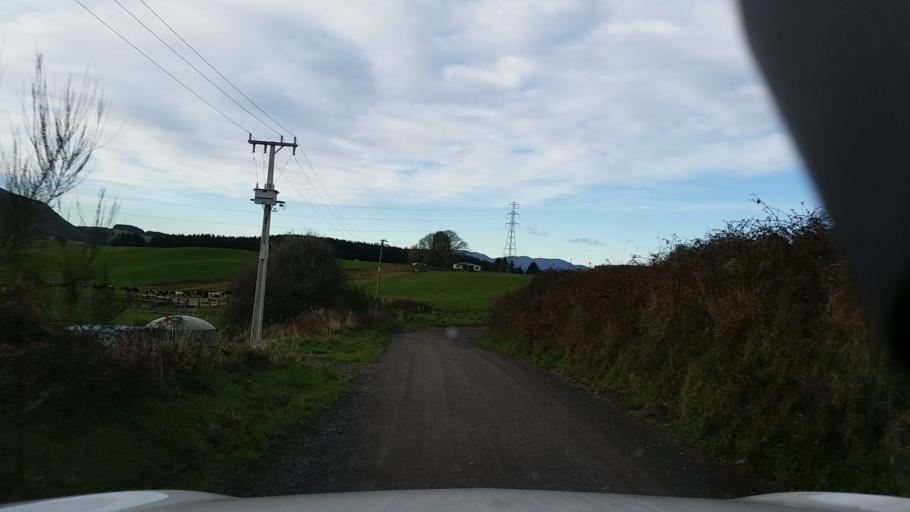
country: NZ
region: Bay of Plenty
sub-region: Rotorua District
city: Rotorua
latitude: -38.2267
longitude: 176.1624
